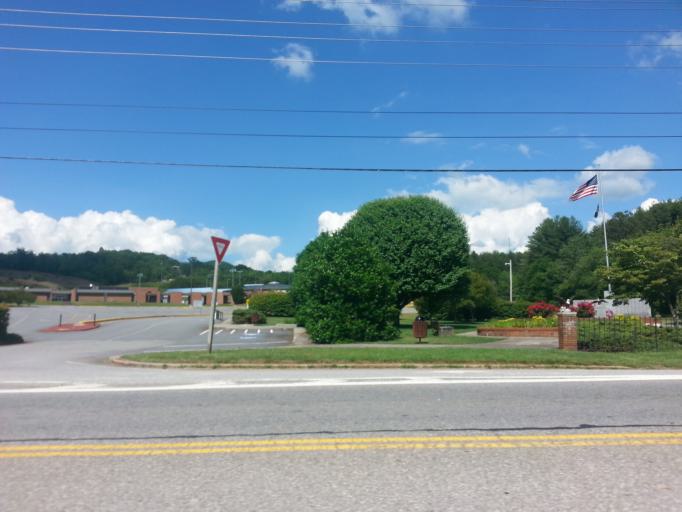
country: US
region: Georgia
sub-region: Towns County
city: Hiawassee
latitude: 34.9293
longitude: -83.7325
